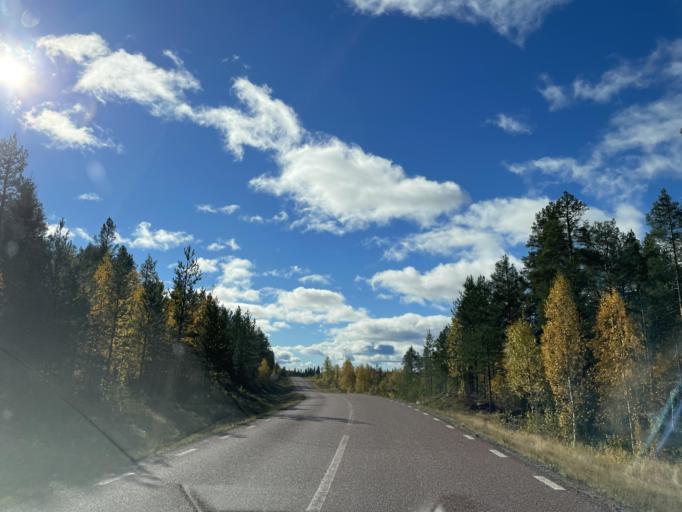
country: NO
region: Hedmark
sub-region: Trysil
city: Innbygda
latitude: 61.5406
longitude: 13.0851
